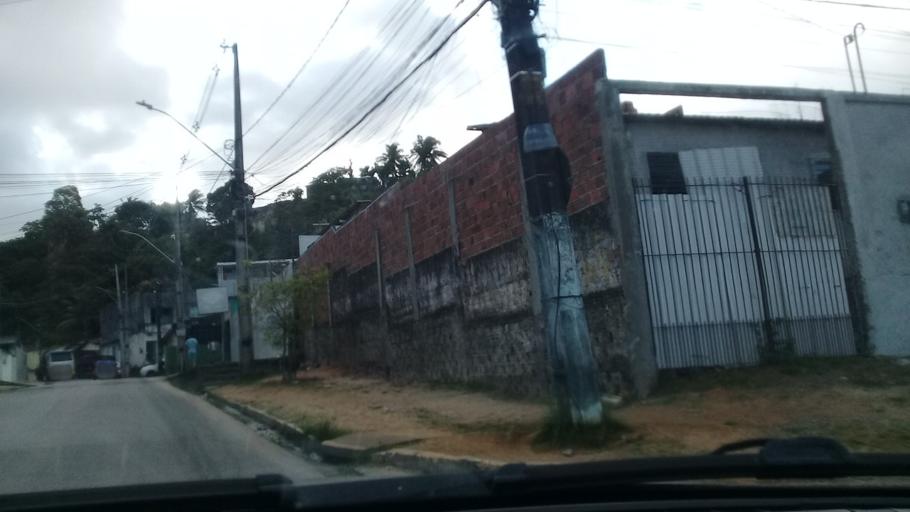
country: BR
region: Pernambuco
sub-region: Jaboatao Dos Guararapes
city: Jaboatao
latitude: -8.1373
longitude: -34.9431
